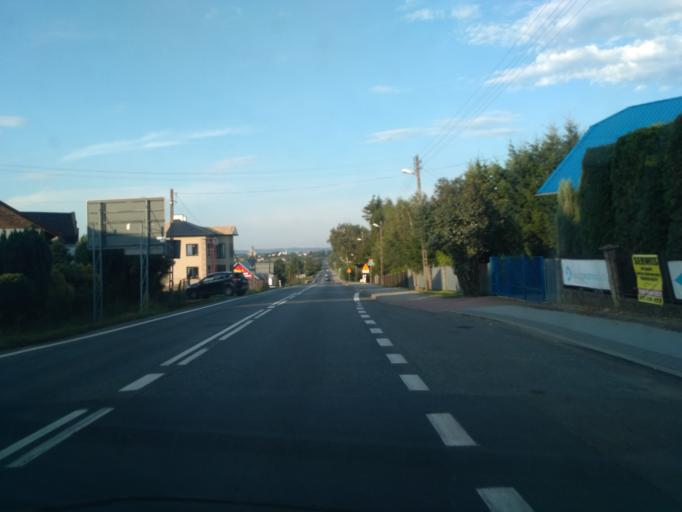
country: PL
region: Subcarpathian Voivodeship
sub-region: Powiat krosnienski
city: Miejsce Piastowe
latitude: 49.6351
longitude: 21.7879
